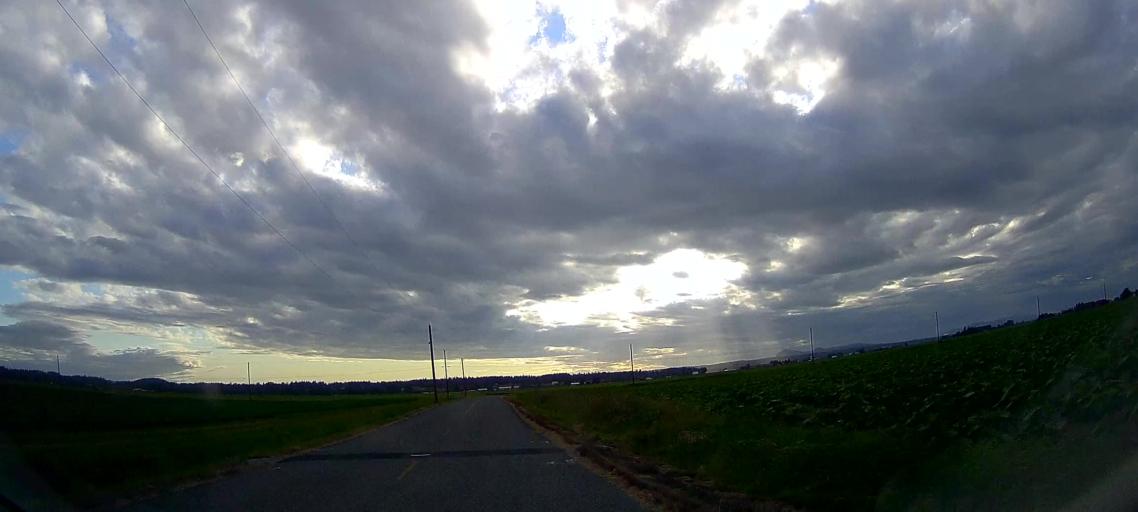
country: US
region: Washington
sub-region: Skagit County
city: Mount Vernon
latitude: 48.3843
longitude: -122.3981
